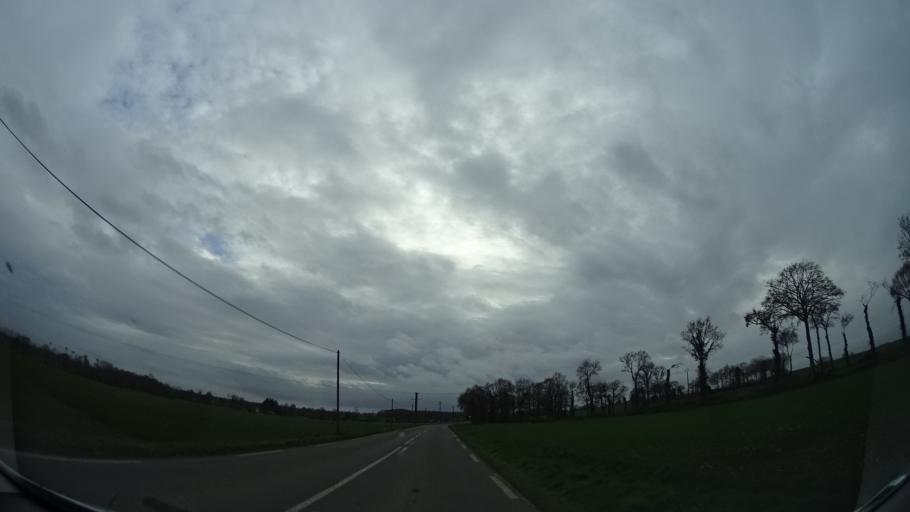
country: FR
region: Brittany
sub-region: Departement des Cotes-d'Armor
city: Evran
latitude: 48.3696
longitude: -1.9703
